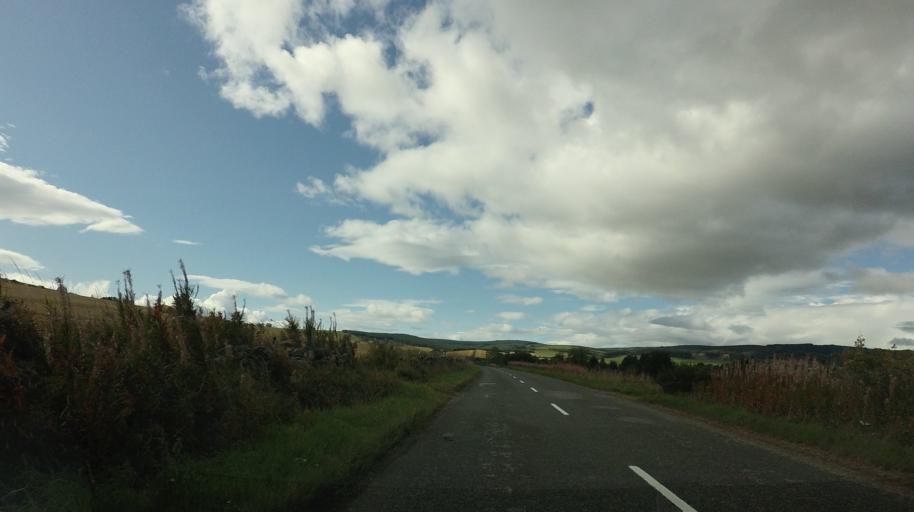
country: GB
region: Scotland
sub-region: Aberdeenshire
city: Alford
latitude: 57.2353
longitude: -2.7340
